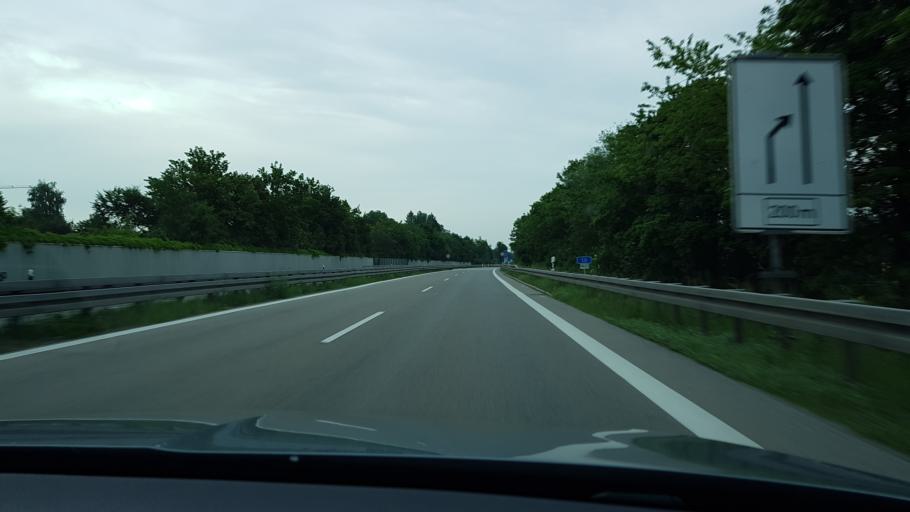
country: DE
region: Bavaria
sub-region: Upper Bavaria
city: Schaftlarn
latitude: 48.0104
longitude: 11.4056
